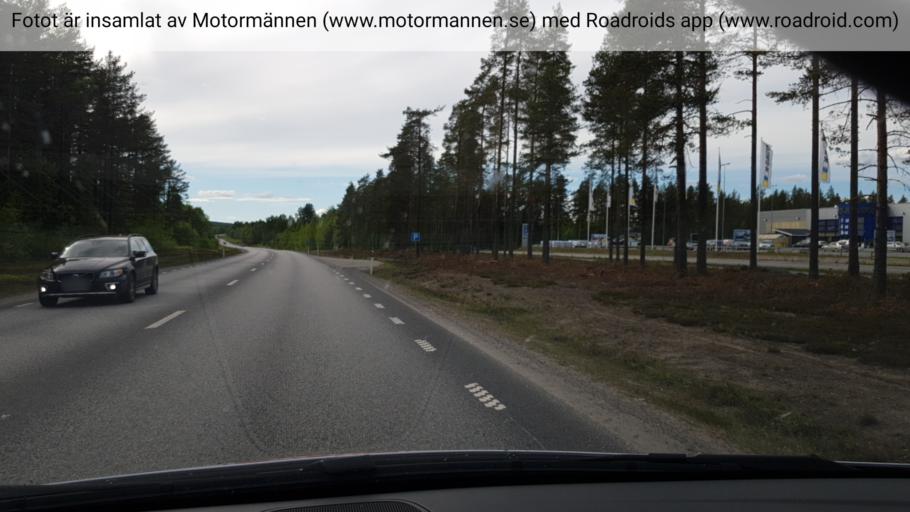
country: SE
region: Vaesterbotten
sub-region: Umea Kommun
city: Roback
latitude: 63.8461
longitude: 20.1551
